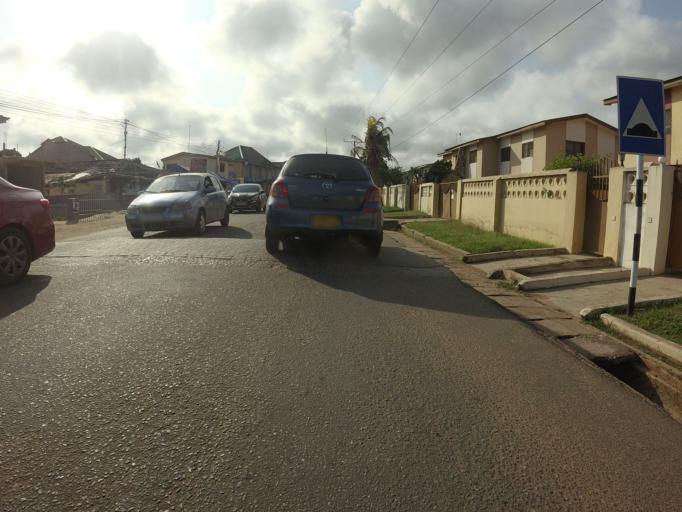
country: GH
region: Greater Accra
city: Nungua
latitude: 5.6152
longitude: -0.0753
